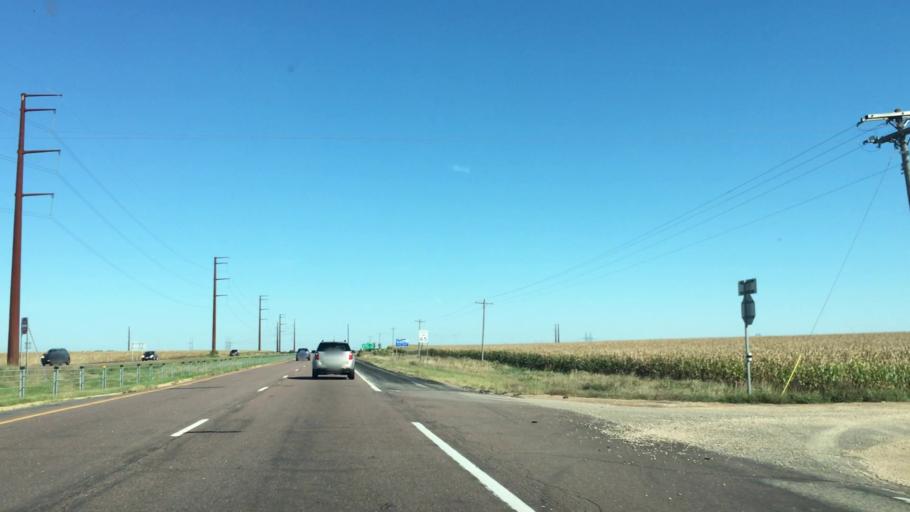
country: US
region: Minnesota
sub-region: Goodhue County
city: Cannon Falls
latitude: 44.6265
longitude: -92.9946
